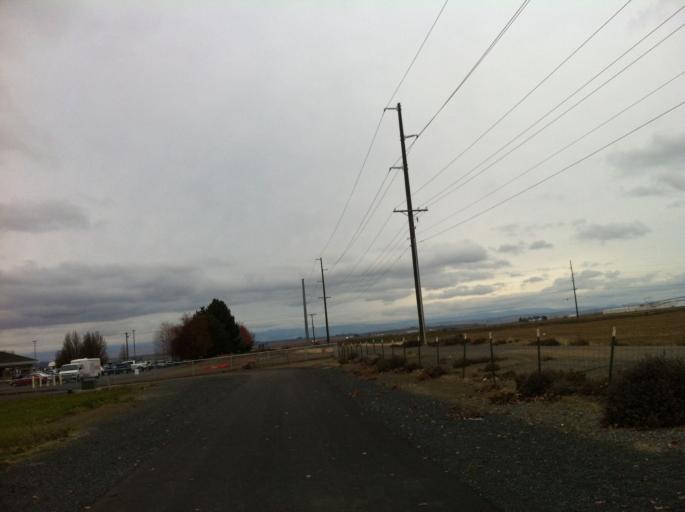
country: US
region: Washington
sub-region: Grant County
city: Quincy
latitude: 47.2267
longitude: -119.8722
